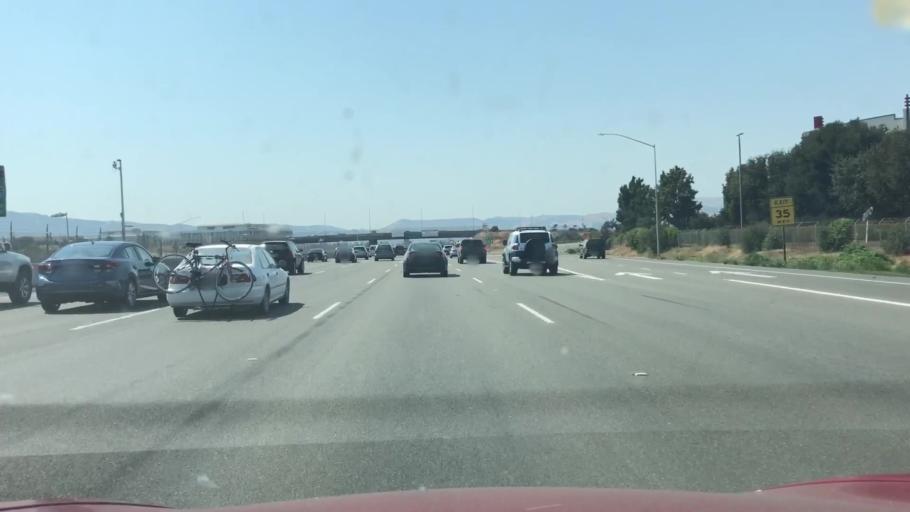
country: US
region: California
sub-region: Alameda County
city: Pleasanton
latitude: 37.7020
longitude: -121.8836
